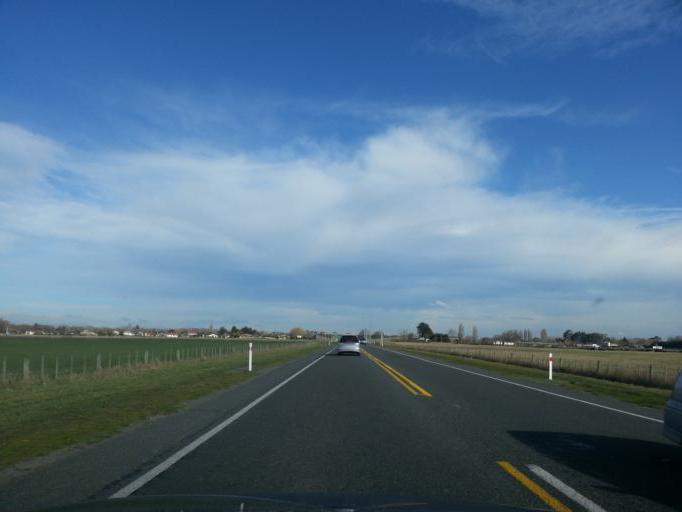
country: NZ
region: Canterbury
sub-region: Waimakariri District
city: Kaiapoi
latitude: -43.3675
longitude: 172.6498
